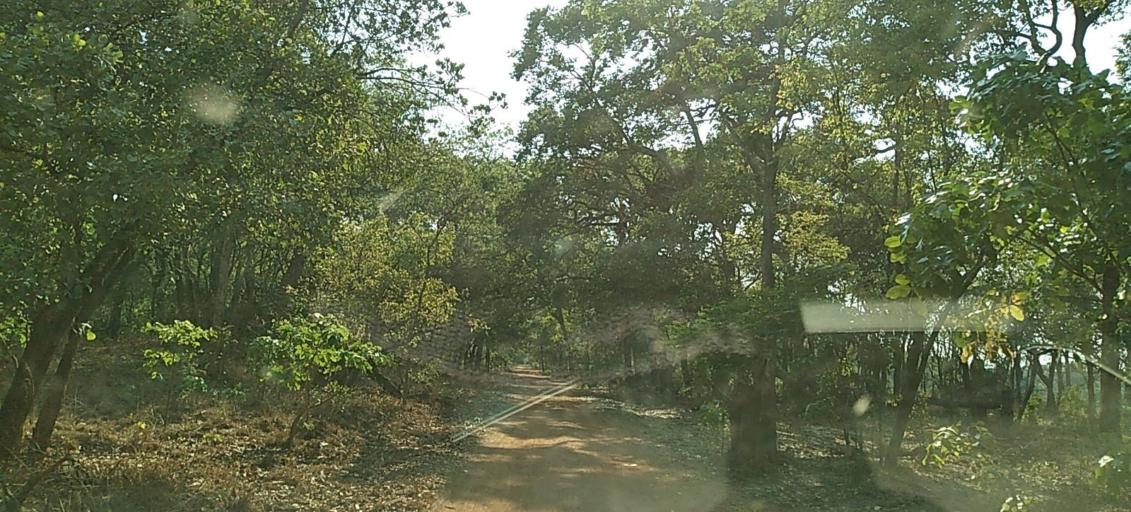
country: ZM
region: Copperbelt
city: Kalulushi
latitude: -13.0053
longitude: 27.7498
